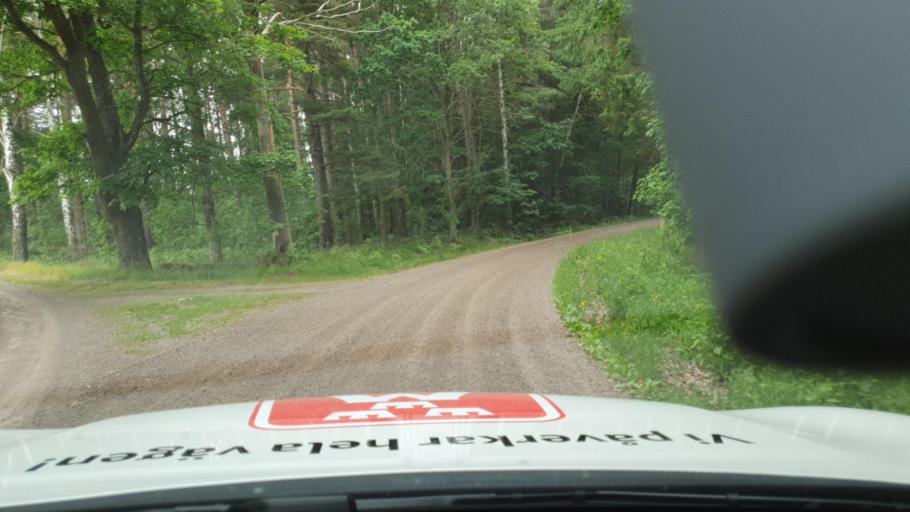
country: SE
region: Vaestra Goetaland
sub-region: Hjo Kommun
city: Hjo
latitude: 58.3861
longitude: 14.3435
